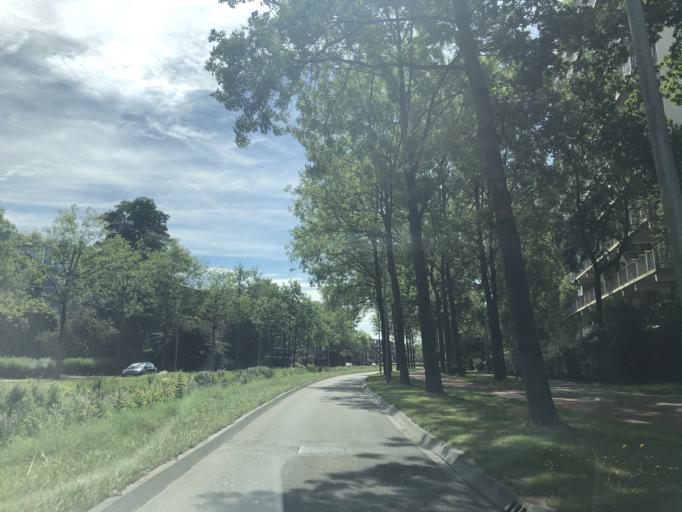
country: NL
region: Gelderland
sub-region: Gemeente Wageningen
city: Wageningen
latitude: 51.9761
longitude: 5.6622
